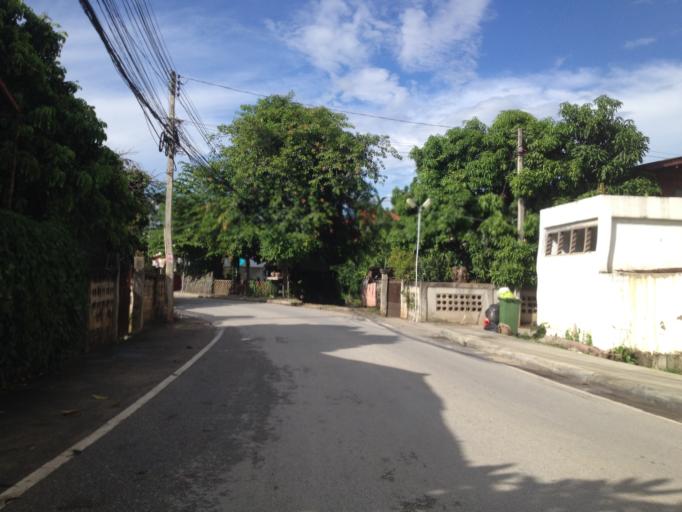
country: TH
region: Chiang Mai
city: Hang Dong
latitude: 18.6873
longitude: 98.9186
